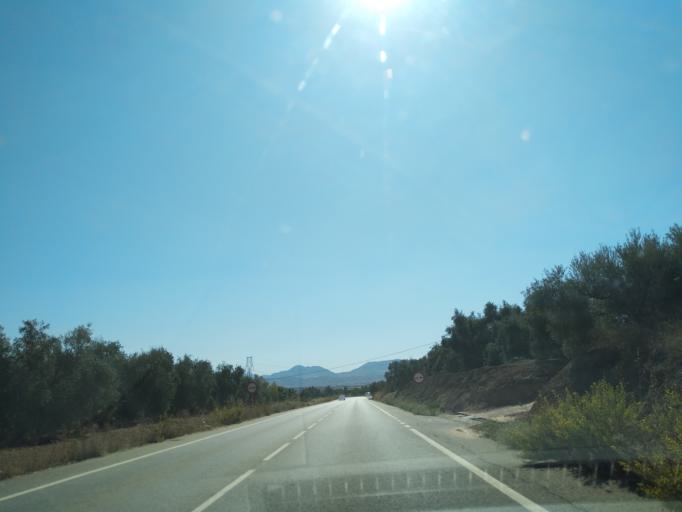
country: ES
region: Andalusia
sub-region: Provincia de Malaga
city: Mollina
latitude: 37.1058
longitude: -4.6380
